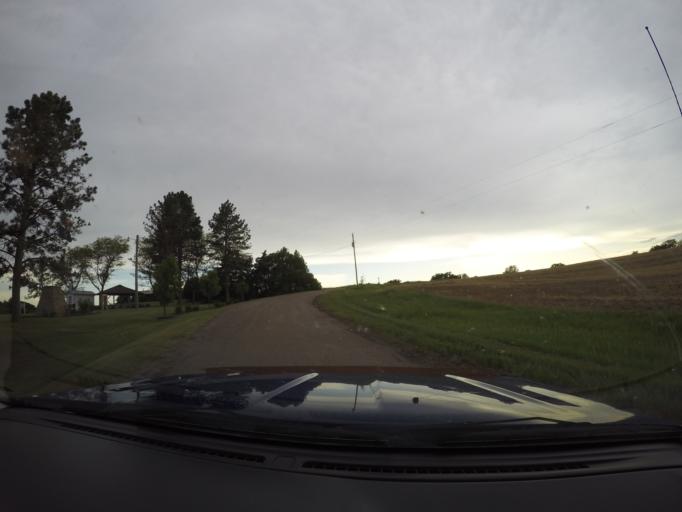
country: US
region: Kansas
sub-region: Smith County
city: Smith Center
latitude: 39.8286
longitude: -98.5795
